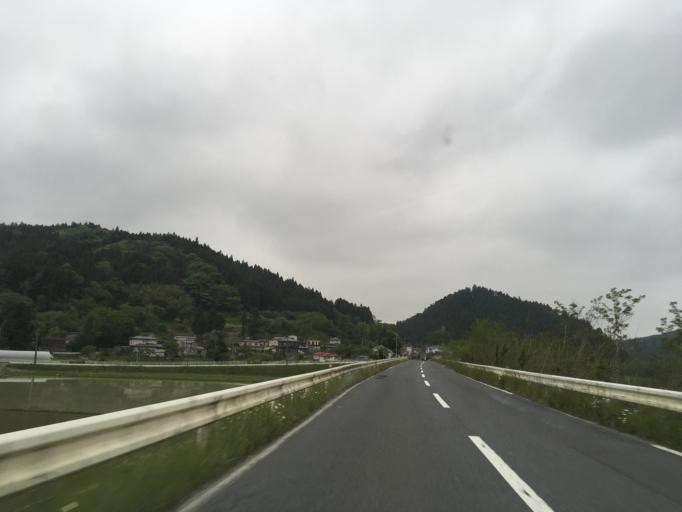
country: JP
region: Iwate
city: Ichinoseki
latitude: 38.7372
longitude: 141.3091
